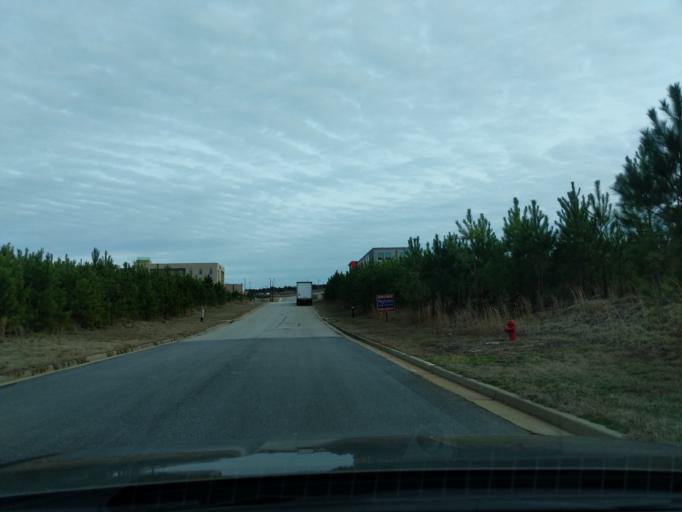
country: US
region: Georgia
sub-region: Columbia County
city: Grovetown
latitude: 33.4823
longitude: -82.2022
